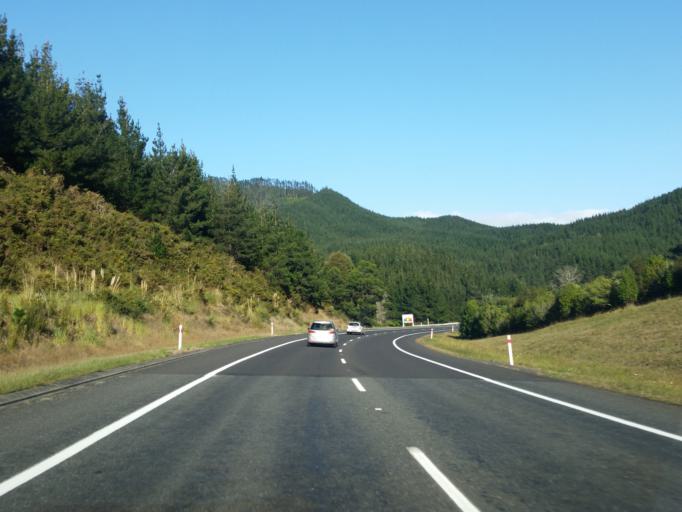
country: NZ
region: Bay of Plenty
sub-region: Western Bay of Plenty District
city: Waihi Beach
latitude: -37.4617
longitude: 175.9180
